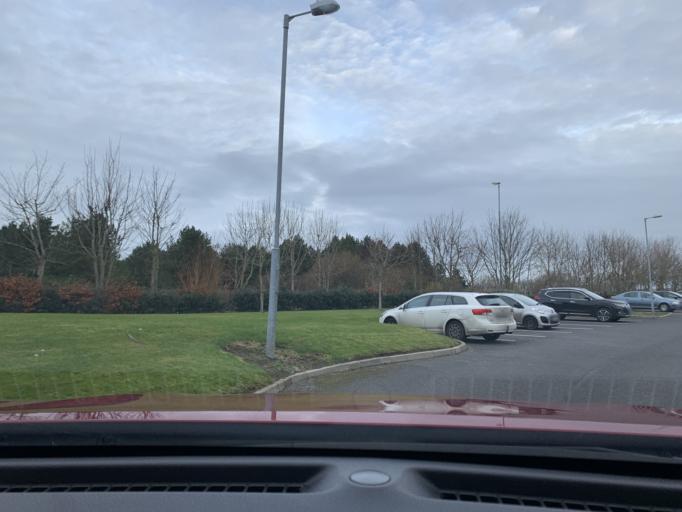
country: IE
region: Connaught
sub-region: Sligo
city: Strandhill
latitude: 54.2769
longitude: -8.5981
